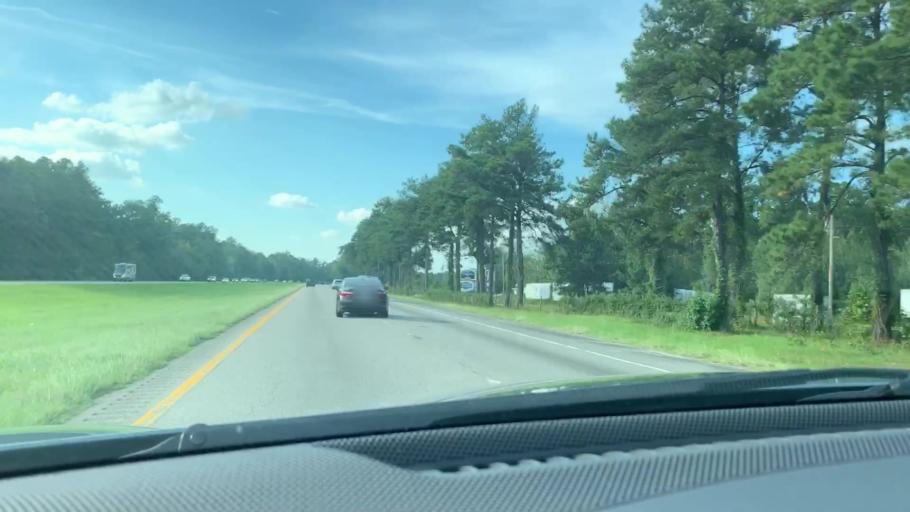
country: US
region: South Carolina
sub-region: Orangeburg County
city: Brookdale
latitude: 33.4710
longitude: -80.7467
